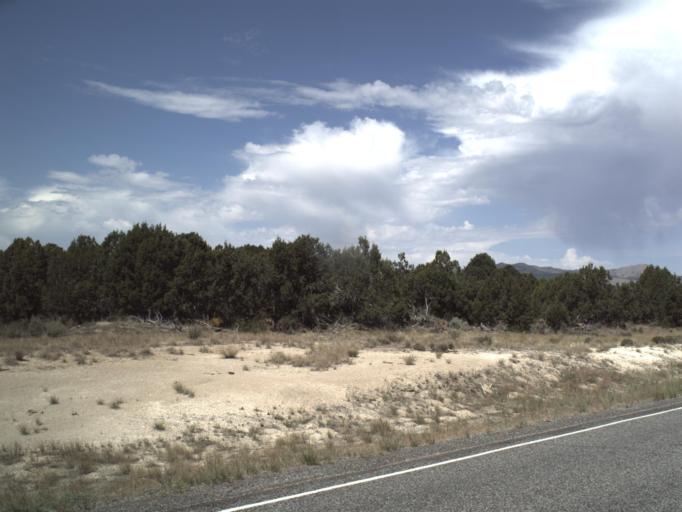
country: US
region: Utah
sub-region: Utah County
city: Genola
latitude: 39.9340
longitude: -112.1734
